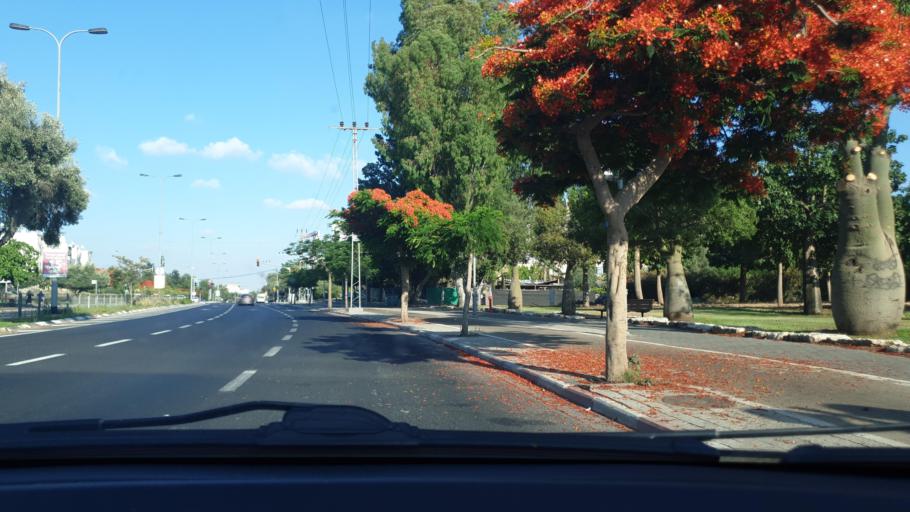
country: IL
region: Tel Aviv
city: Giv`atayim
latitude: 32.0570
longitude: 34.8052
